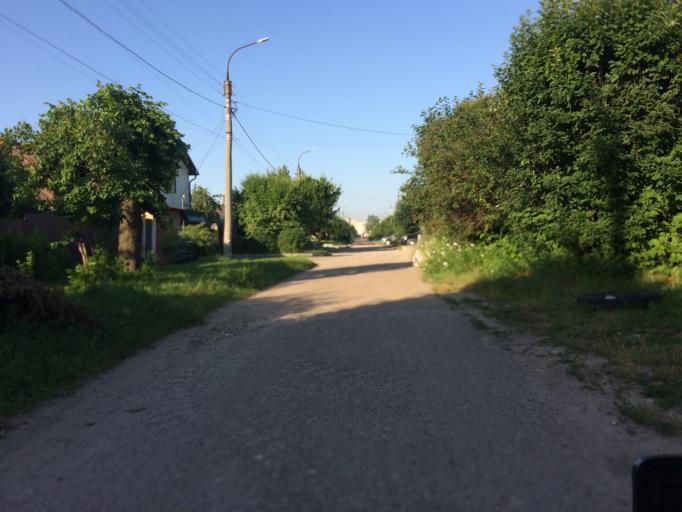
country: RU
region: Mariy-El
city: Yoshkar-Ola
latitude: 56.6493
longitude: 47.9082
